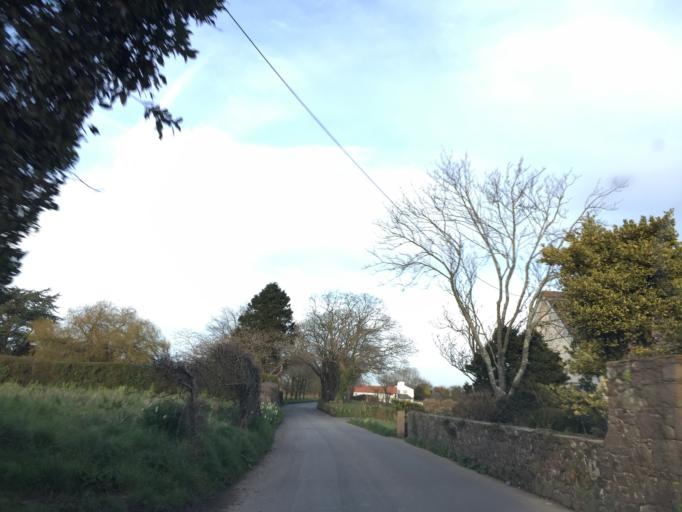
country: JE
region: St Helier
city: Saint Helier
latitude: 49.2284
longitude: -2.0630
